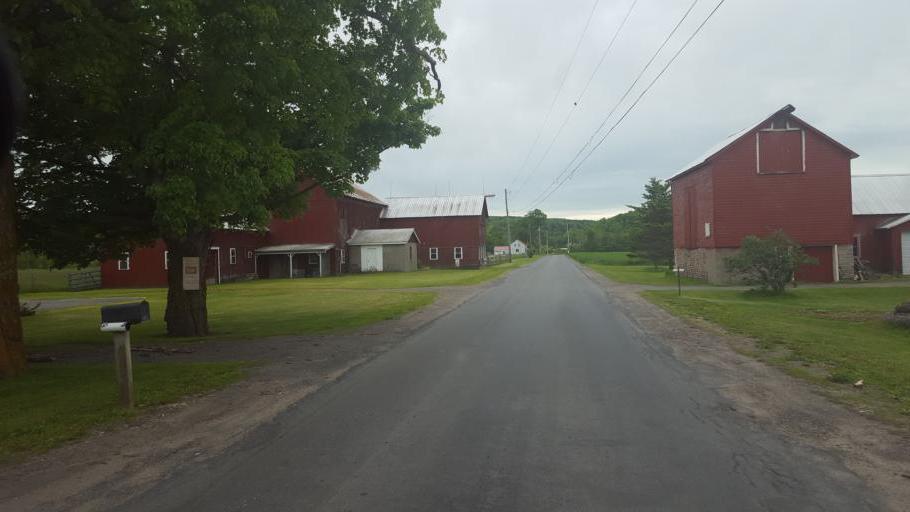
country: US
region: New York
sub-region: Oneida County
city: Chadwicks
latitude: 42.8883
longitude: -75.1650
